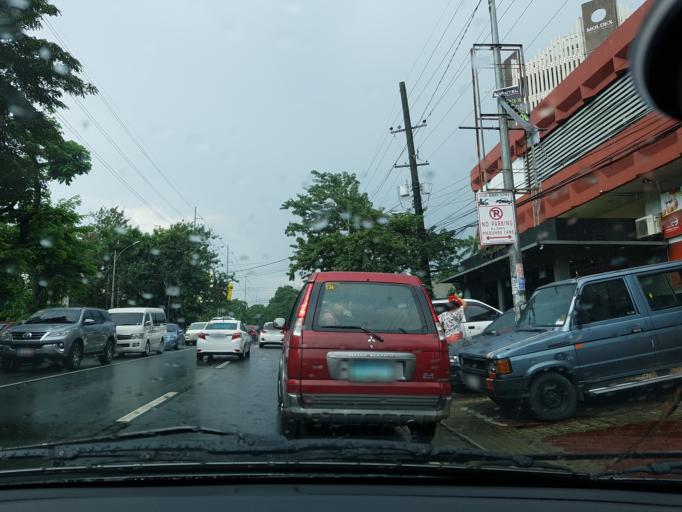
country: PH
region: Calabarzon
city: Del Monte
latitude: 14.6395
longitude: 121.0263
